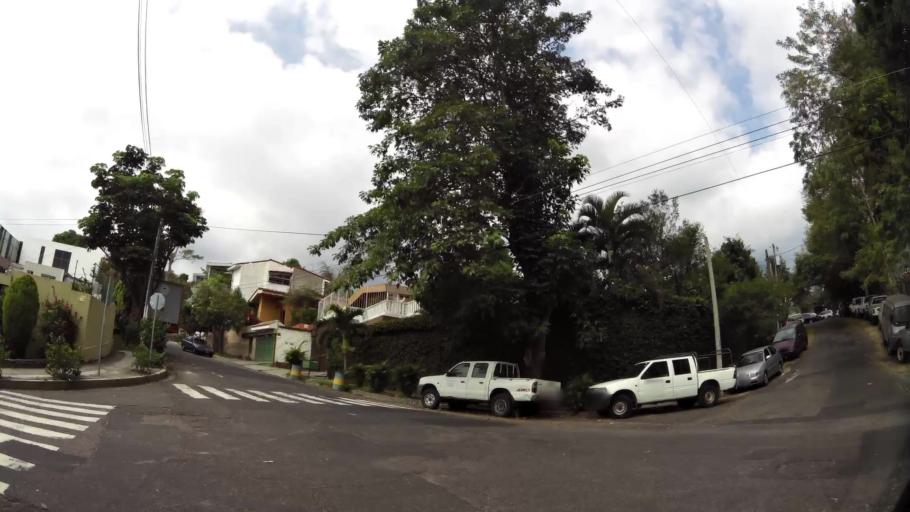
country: SV
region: La Libertad
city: Santa Tecla
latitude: 13.7076
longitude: -89.2507
